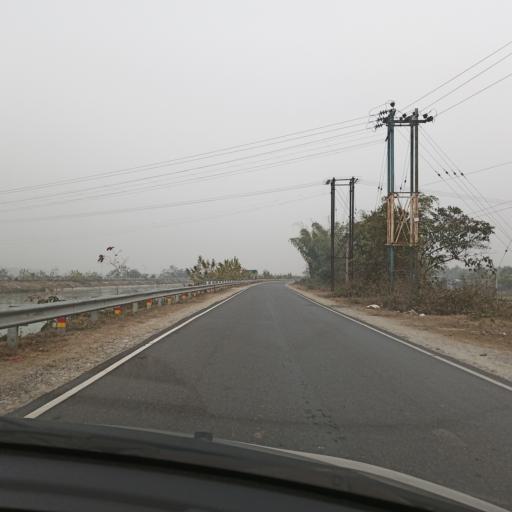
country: IN
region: West Bengal
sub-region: Jalpaiguri
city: Odlabari
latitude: 26.7350
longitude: 88.5753
